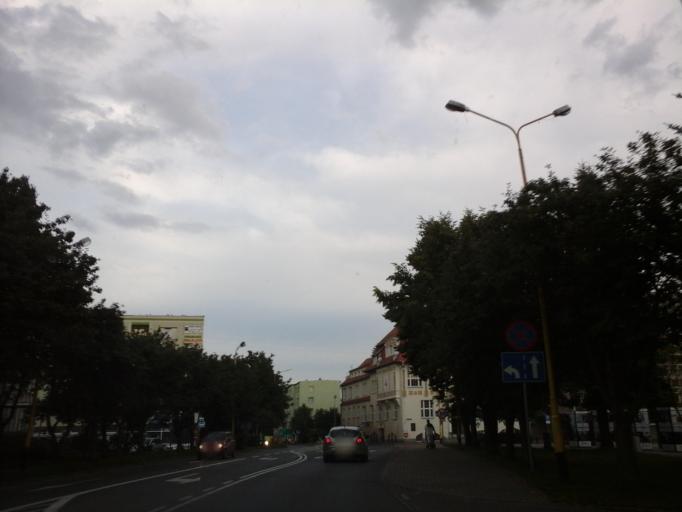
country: PL
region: West Pomeranian Voivodeship
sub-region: Powiat goleniowski
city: Nowogard
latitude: 53.6718
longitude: 15.1191
